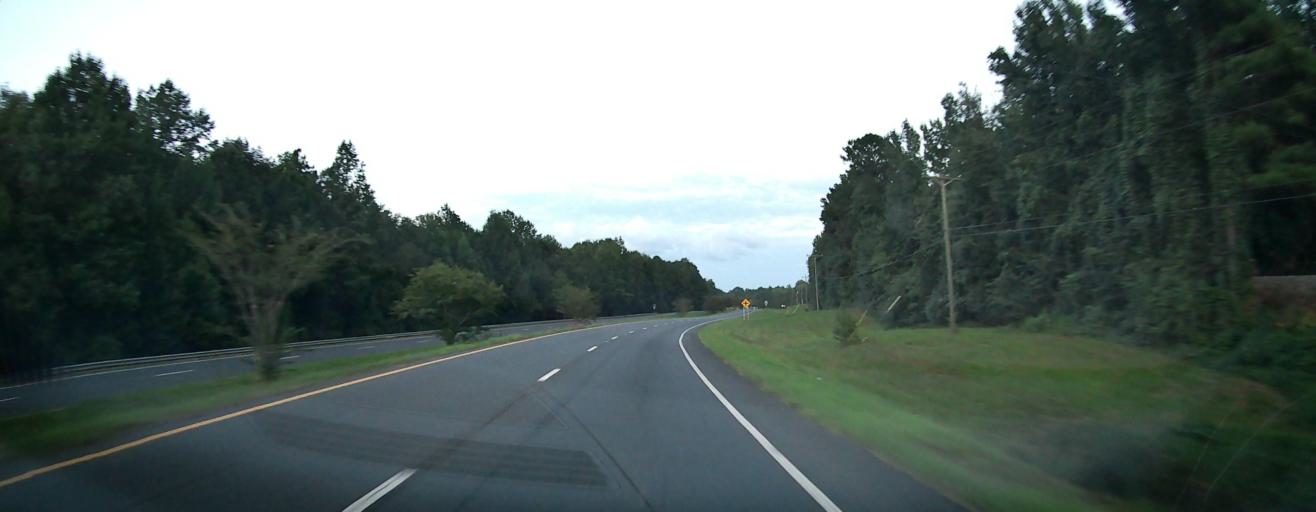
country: US
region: Georgia
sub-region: Muscogee County
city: Columbus
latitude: 32.5503
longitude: -84.7842
